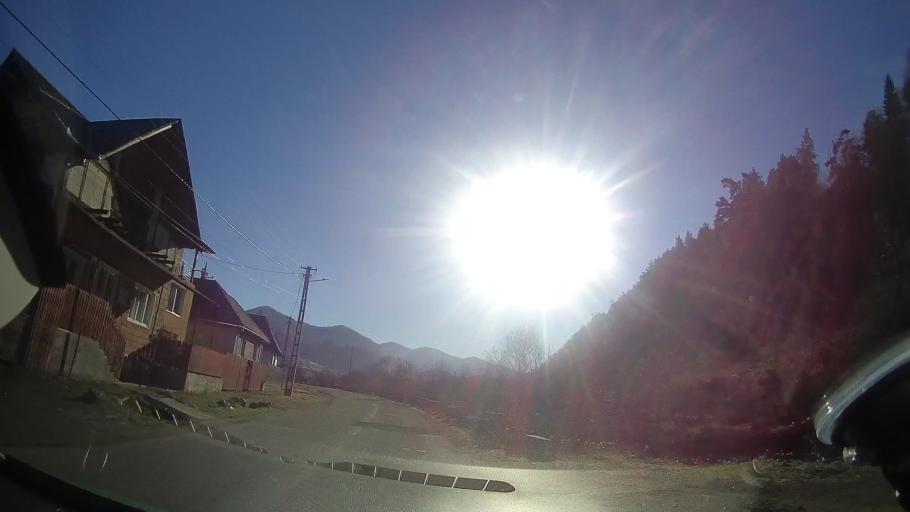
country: RO
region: Cluj
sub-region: Comuna Sacueu
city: Sacuieu
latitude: 46.8244
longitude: 22.8850
